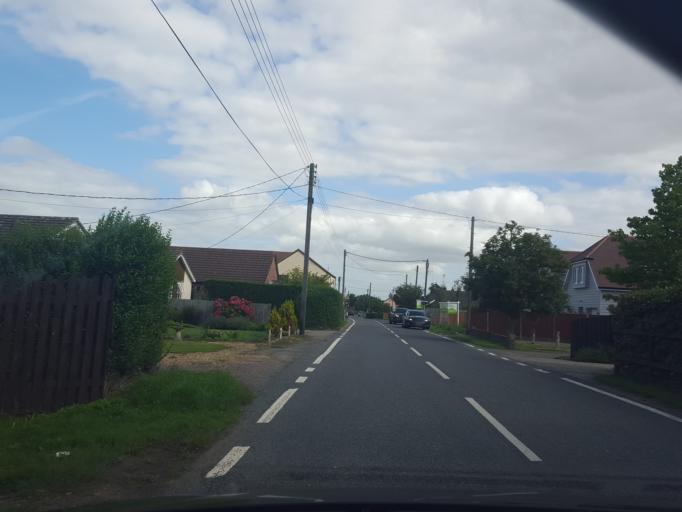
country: GB
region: England
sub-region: Essex
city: Mistley
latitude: 51.9253
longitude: 1.1025
